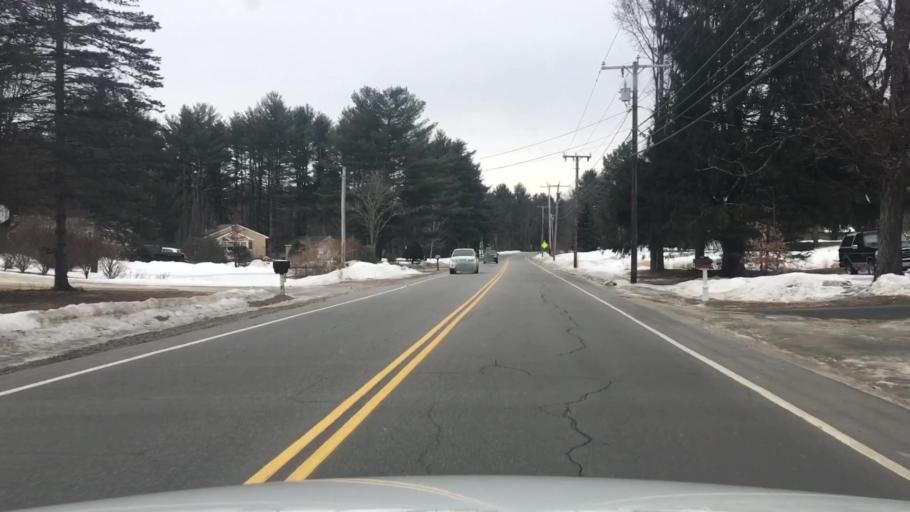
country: US
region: New Hampshire
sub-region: Strafford County
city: Rochester
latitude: 43.3715
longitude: -70.9841
